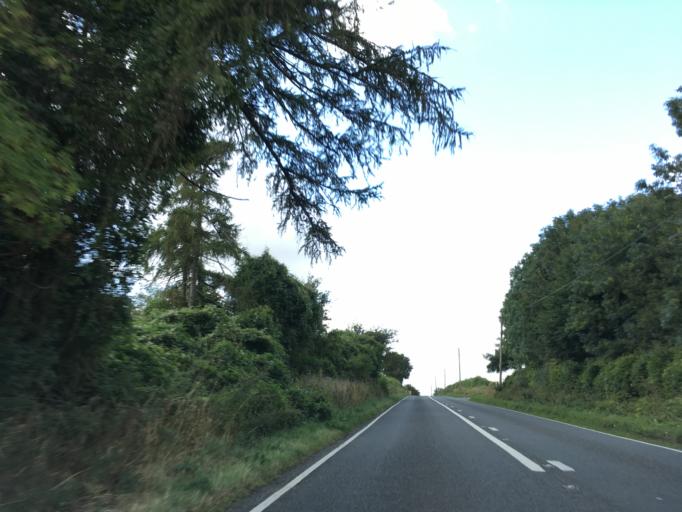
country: GB
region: England
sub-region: Hampshire
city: Kings Worthy
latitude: 51.1433
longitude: -1.3760
